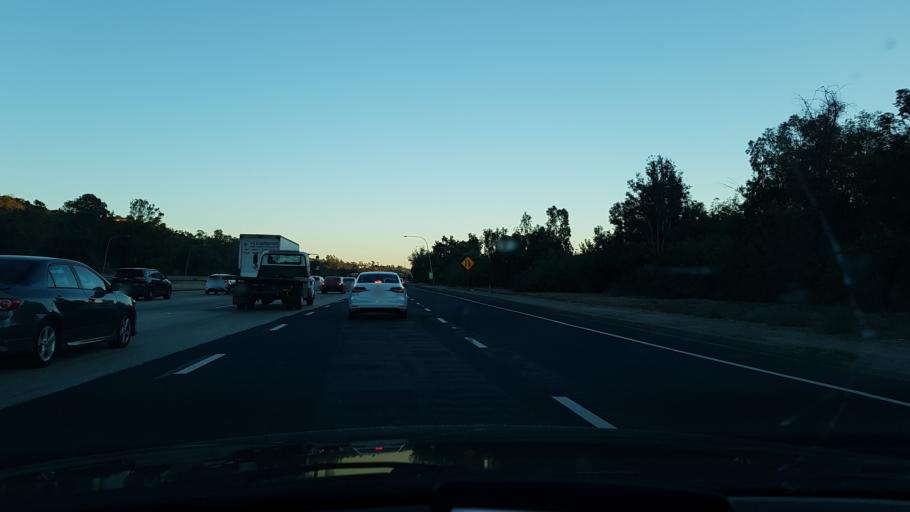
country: US
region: California
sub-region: San Diego County
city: La Mesa
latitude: 32.8201
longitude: -117.1162
